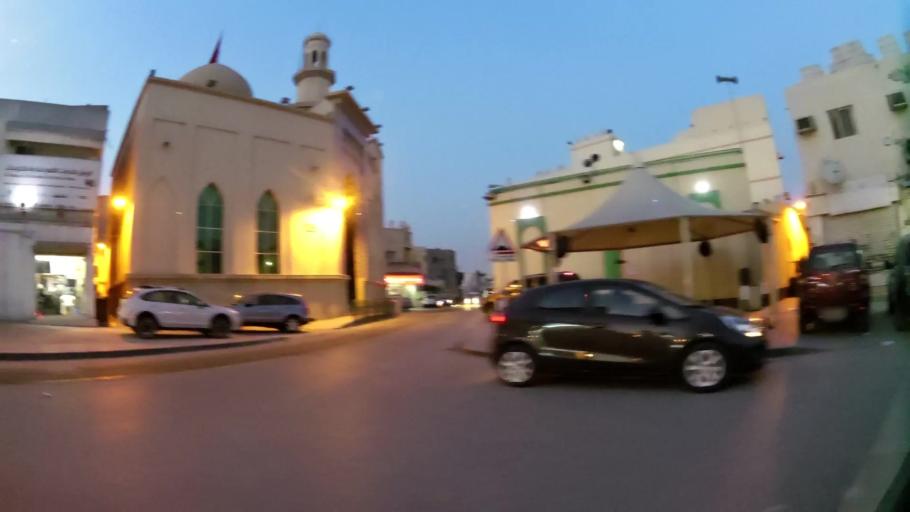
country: BH
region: Manama
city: Jidd Hafs
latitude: 26.2048
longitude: 50.5527
